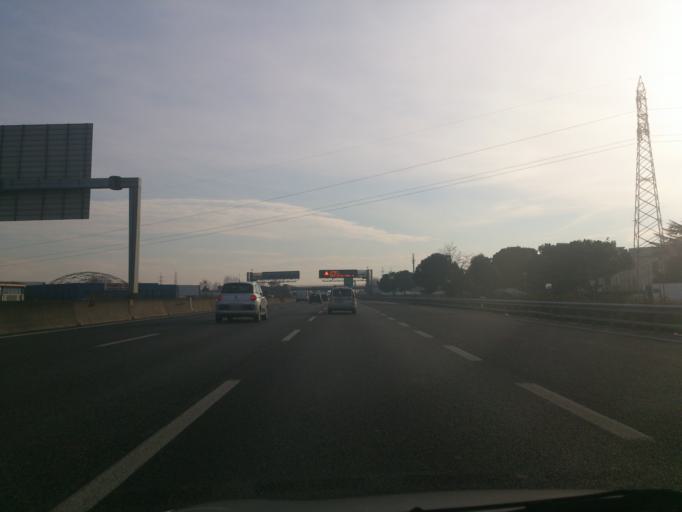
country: IT
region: Lombardy
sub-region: Citta metropolitana di Milano
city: Civesio
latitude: 45.4021
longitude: 9.2608
